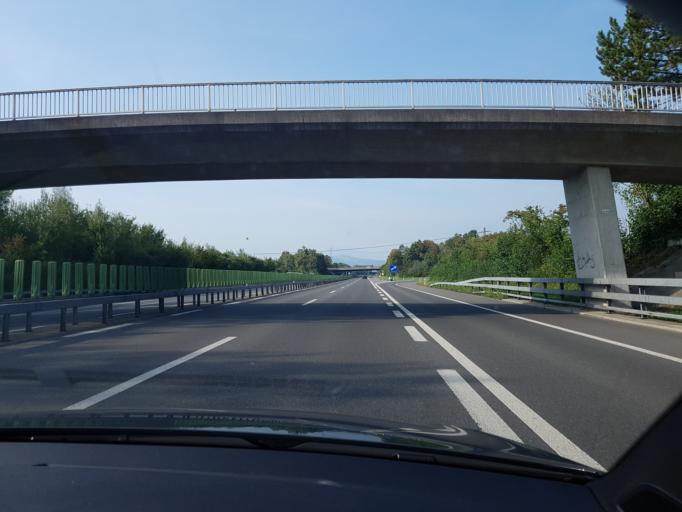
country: CH
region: Zug
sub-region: Zug
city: Baar
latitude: 47.1977
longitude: 8.5138
